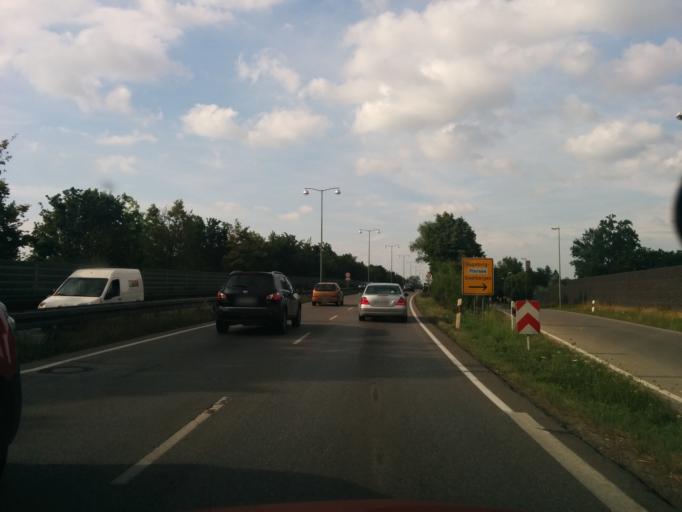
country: DE
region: Bavaria
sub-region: Swabia
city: Stadtbergen
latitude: 48.3588
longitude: 10.8511
